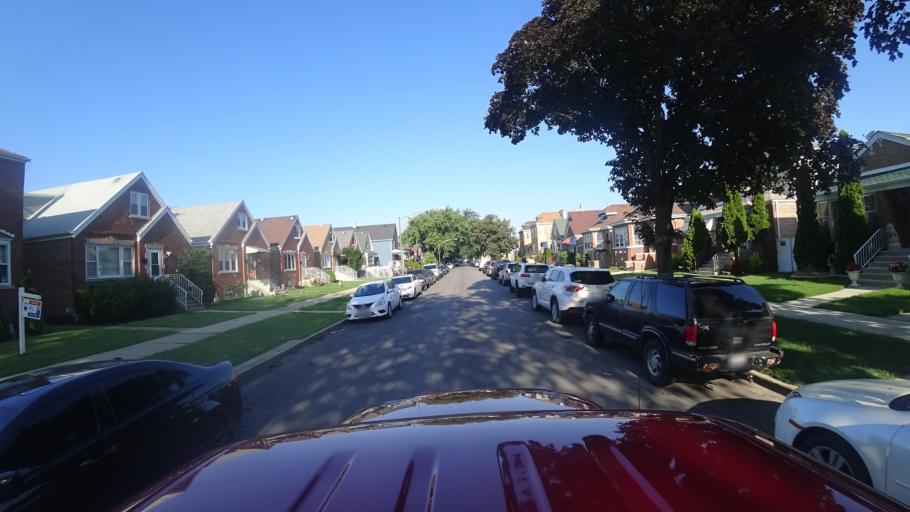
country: US
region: Illinois
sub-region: Cook County
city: Hometown
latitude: 41.7888
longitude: -87.7160
